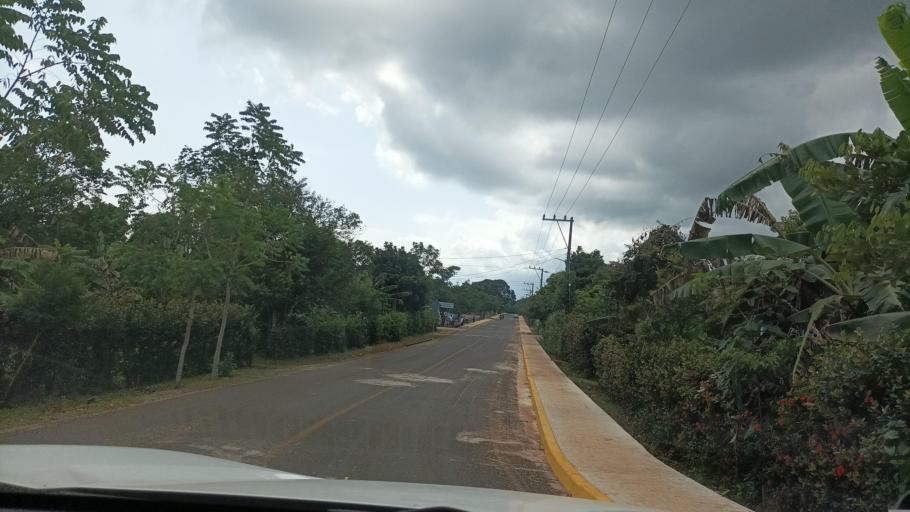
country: MX
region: Veracruz
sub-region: Pajapan
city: Pajapan
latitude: 18.1858
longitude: -94.6723
